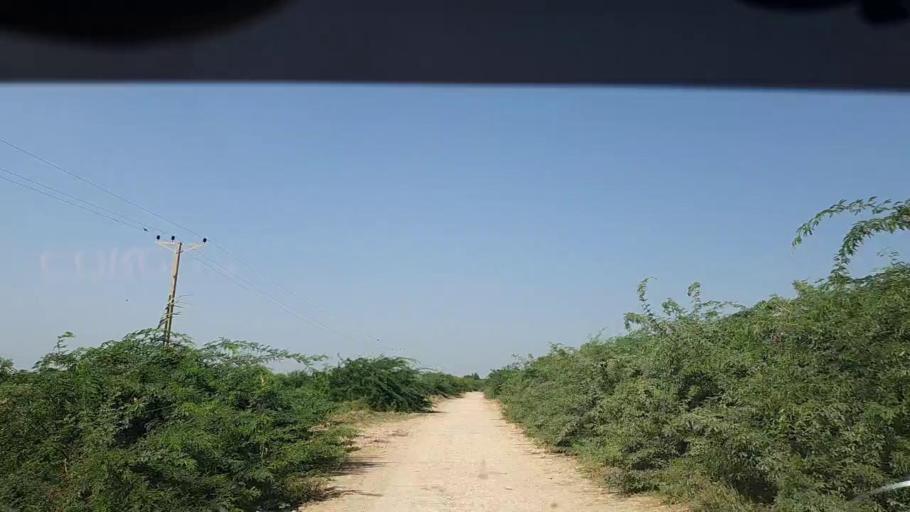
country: PK
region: Sindh
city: Badin
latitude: 24.4666
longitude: 68.7798
